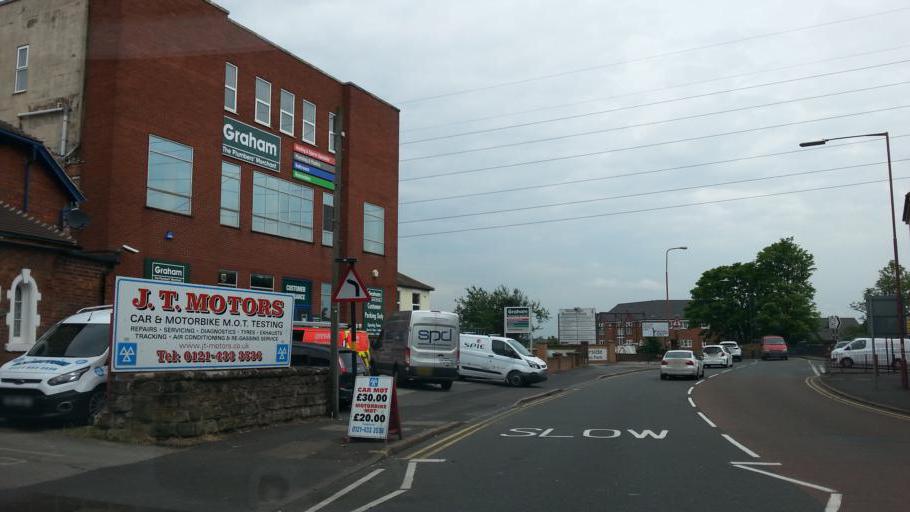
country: GB
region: England
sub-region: City and Borough of Birmingham
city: Birmingham
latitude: 52.4202
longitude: -1.9220
